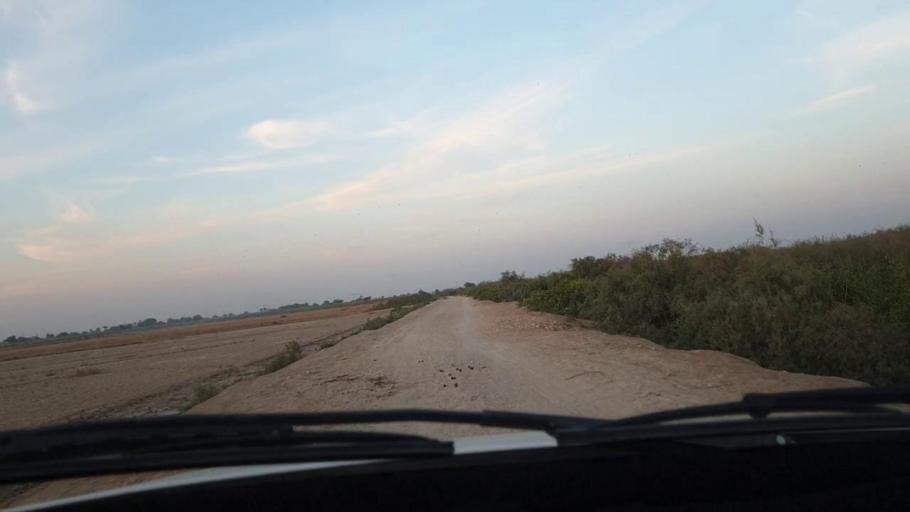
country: PK
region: Sindh
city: Tando Muhammad Khan
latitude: 25.0932
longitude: 68.3877
